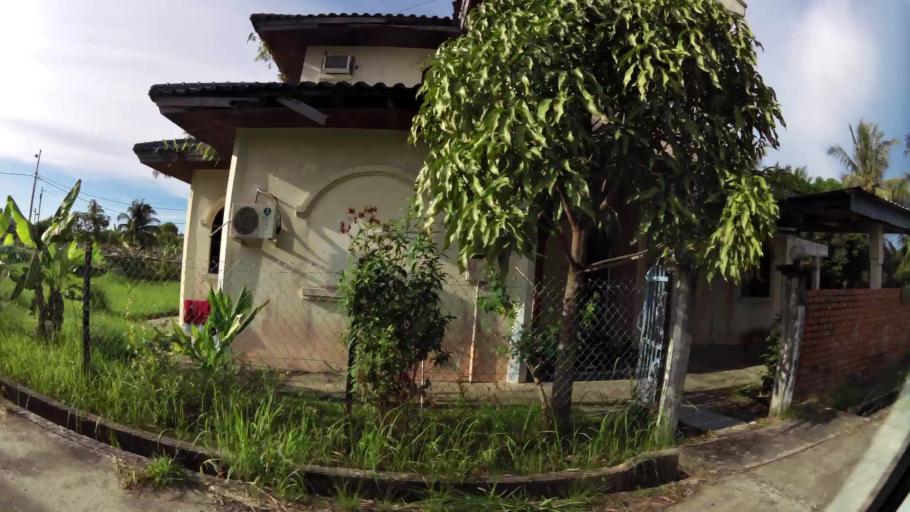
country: BN
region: Brunei and Muara
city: Bandar Seri Begawan
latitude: 4.9616
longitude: 115.0249
